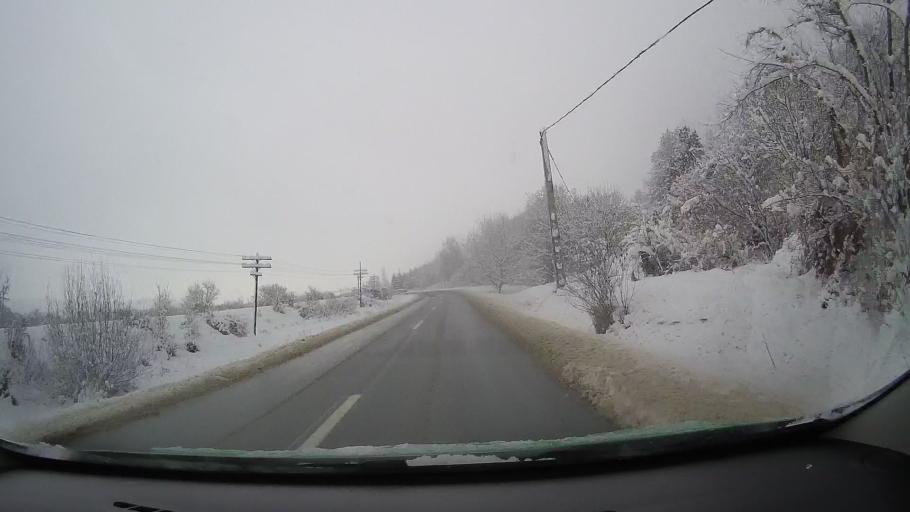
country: RO
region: Sibiu
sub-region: Comuna Orlat
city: Orlat
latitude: 45.7581
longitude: 23.9433
